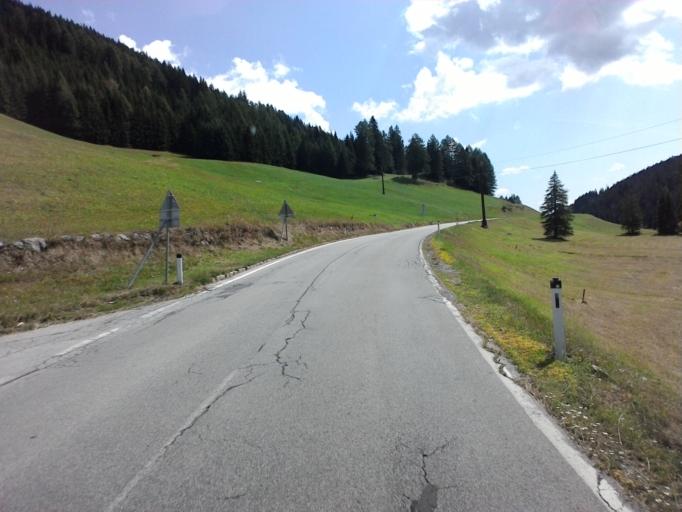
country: AT
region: Tyrol
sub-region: Politischer Bezirk Lienz
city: Kartitsch
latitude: 46.7198
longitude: 12.5264
